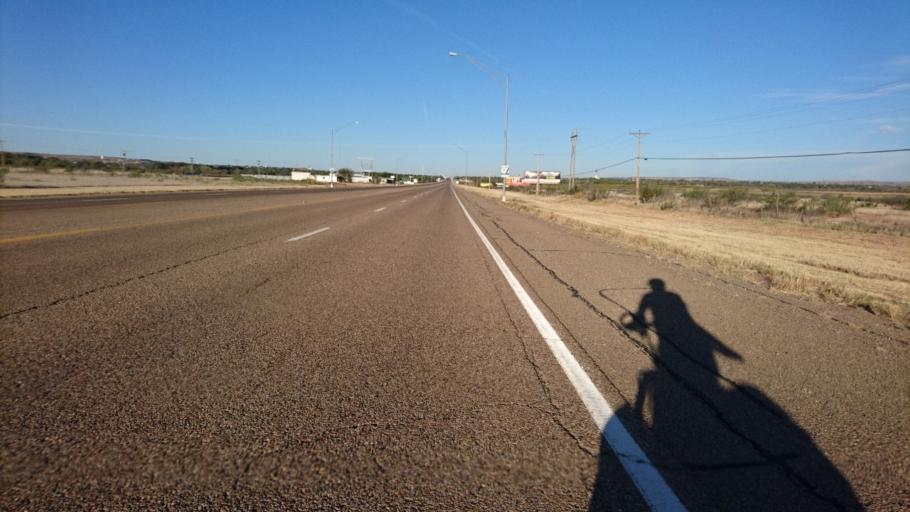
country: US
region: New Mexico
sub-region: Quay County
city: Tucumcari
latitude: 35.1720
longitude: -103.6870
